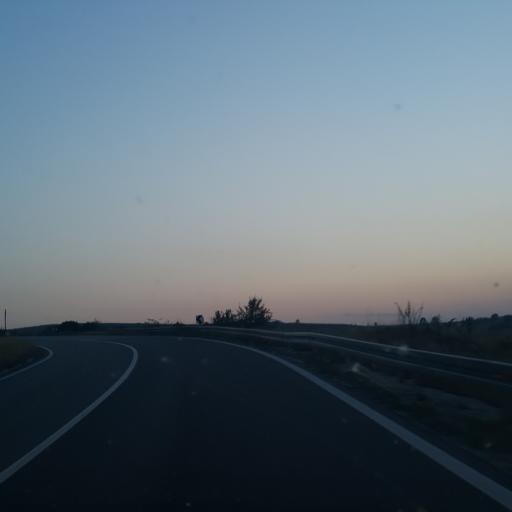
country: RS
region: Central Serbia
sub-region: Nisavski Okrug
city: Svrljig
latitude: 43.4321
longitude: 22.1602
